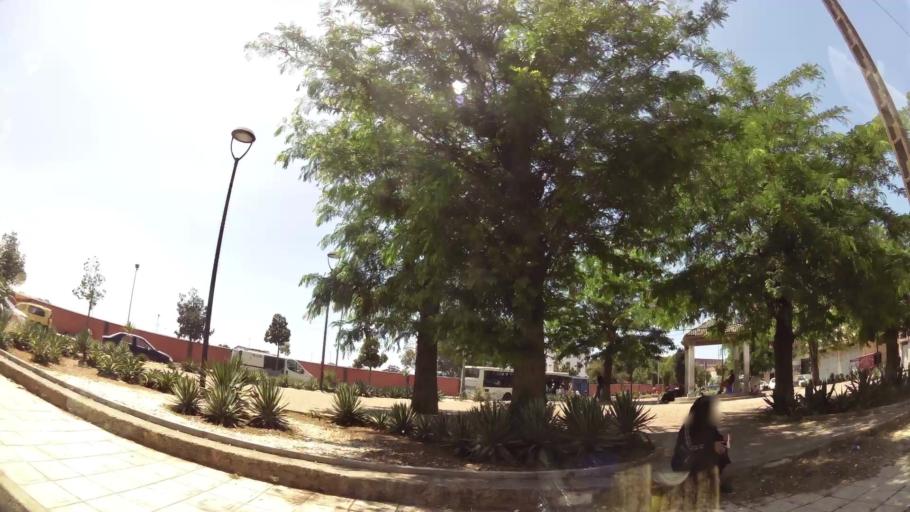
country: MA
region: Gharb-Chrarda-Beni Hssen
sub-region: Kenitra Province
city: Kenitra
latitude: 34.2548
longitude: -6.5598
